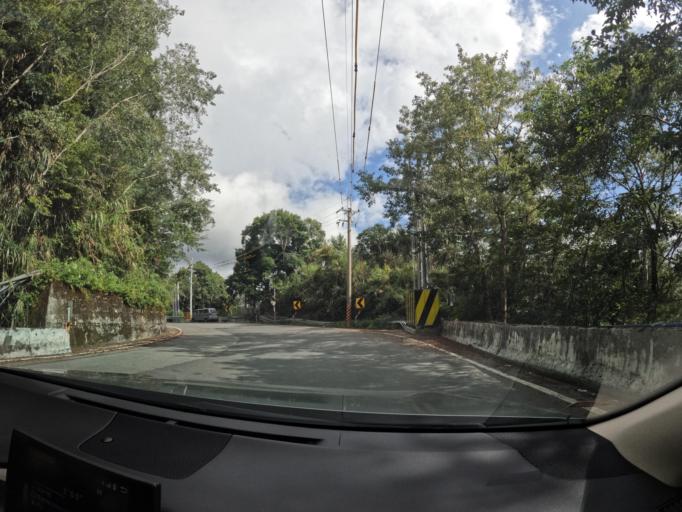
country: TW
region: Taiwan
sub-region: Taitung
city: Taitung
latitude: 23.2225
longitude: 121.0110
